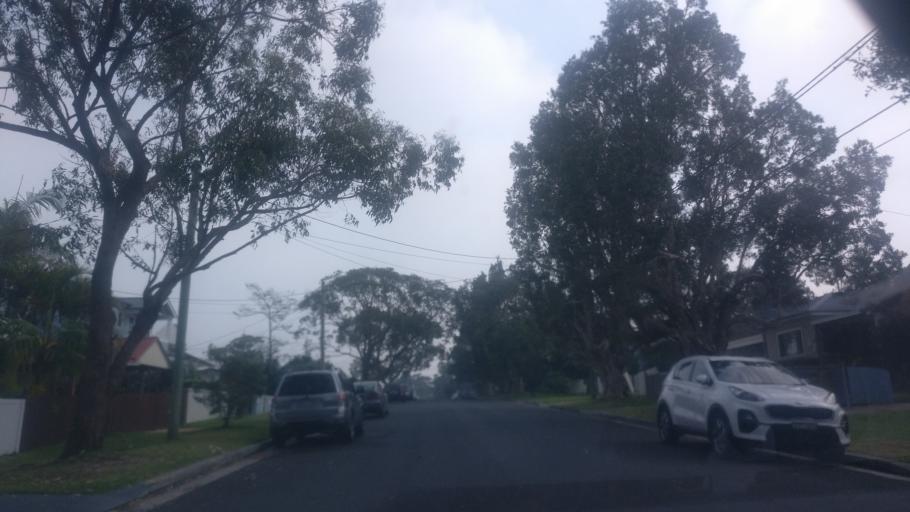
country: AU
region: New South Wales
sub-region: Warringah
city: Narrabeen
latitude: -33.7300
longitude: 151.2906
